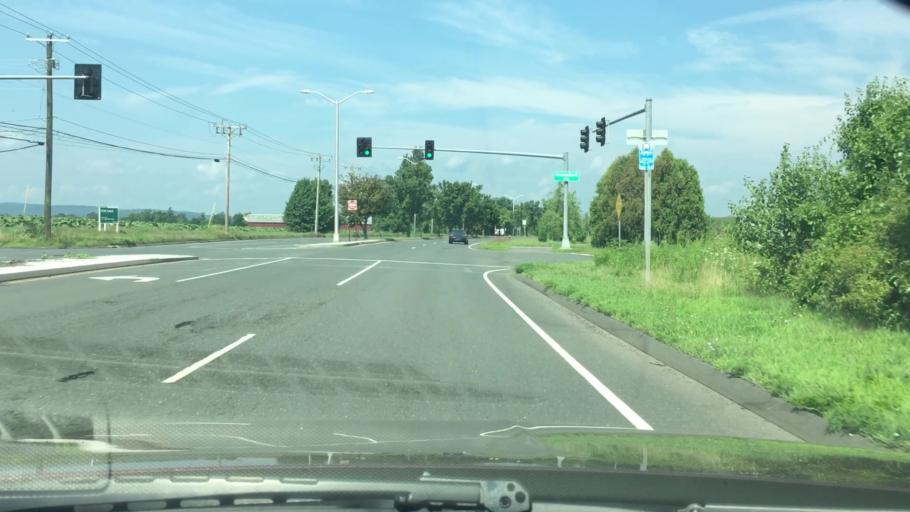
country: US
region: Connecticut
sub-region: Hartford County
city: Windsor
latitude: 41.8761
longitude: -72.6944
